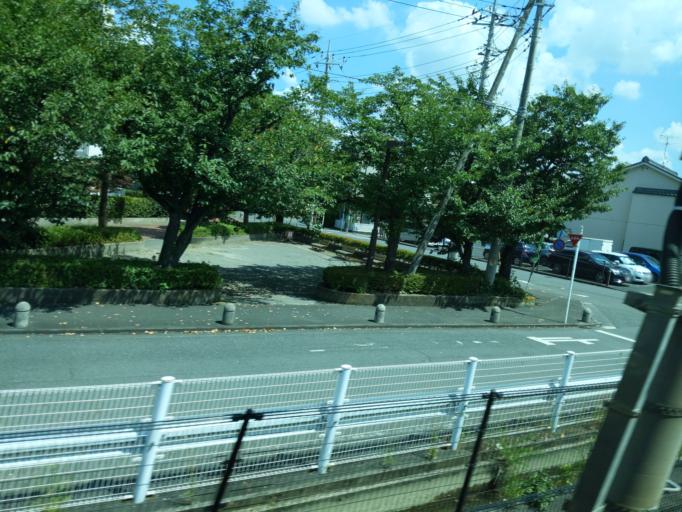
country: JP
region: Tokyo
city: Chofugaoka
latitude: 35.6383
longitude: 139.5264
